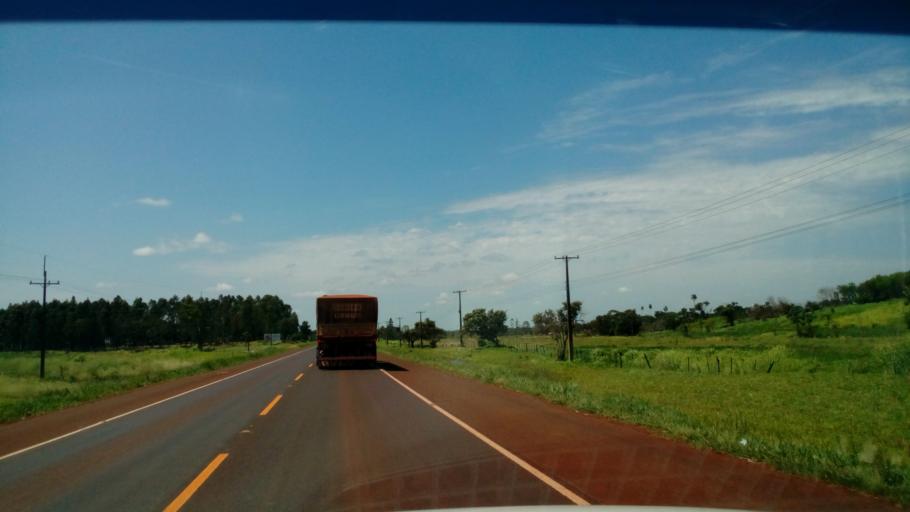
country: PY
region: Alto Parana
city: Colonia Yguazu
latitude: -25.5119
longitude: -54.8994
